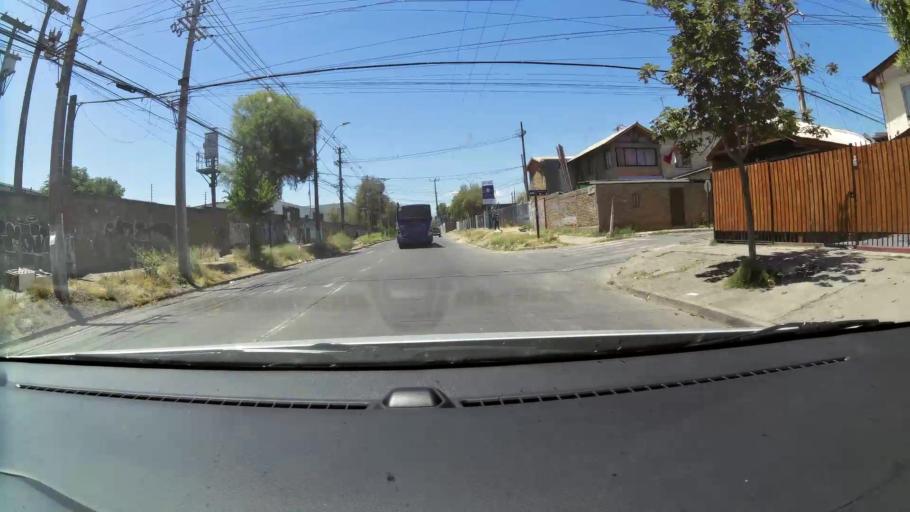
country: CL
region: Santiago Metropolitan
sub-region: Provincia de Maipo
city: San Bernardo
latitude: -33.6174
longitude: -70.7022
